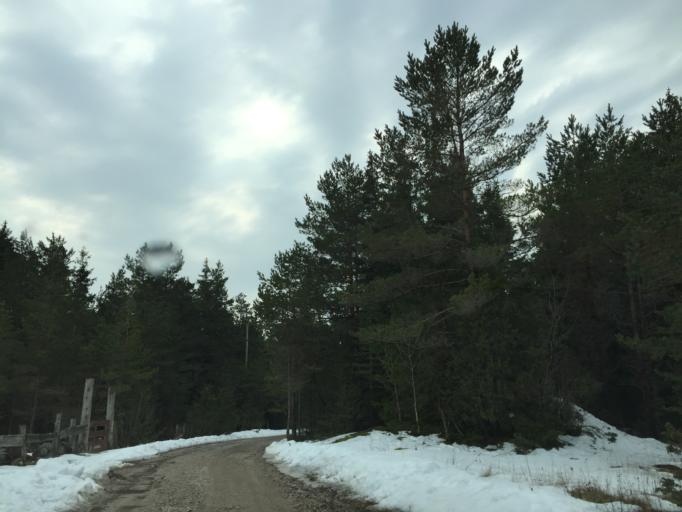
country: EE
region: Saare
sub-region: Kuressaare linn
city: Kuressaare
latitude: 58.4405
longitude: 22.1341
